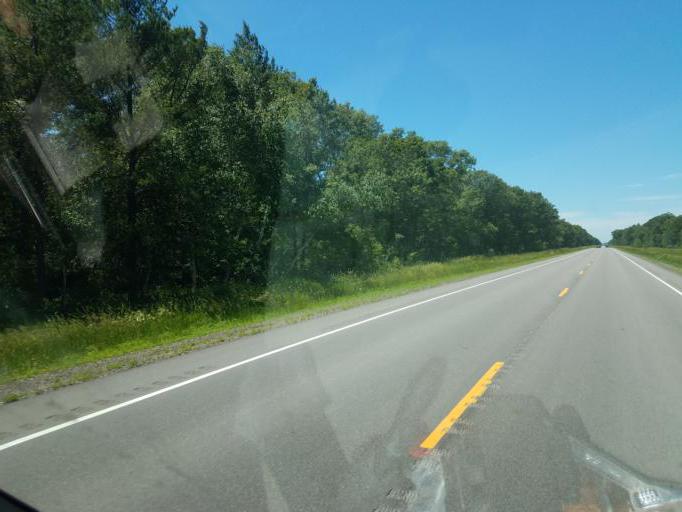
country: US
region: Wisconsin
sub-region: Juneau County
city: New Lisbon
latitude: 44.0255
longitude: -90.2129
